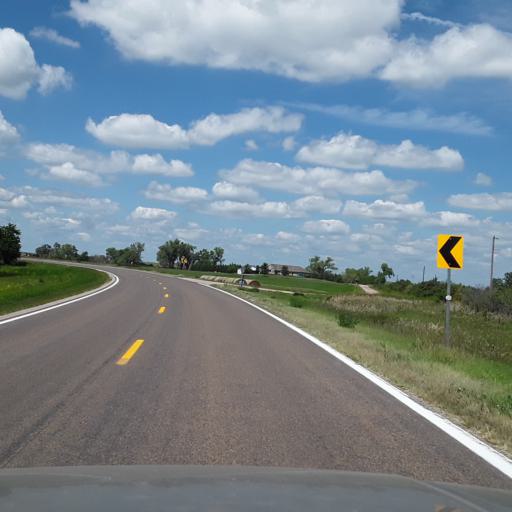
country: US
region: Nebraska
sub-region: Nance County
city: Genoa
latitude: 41.3322
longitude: -97.6756
